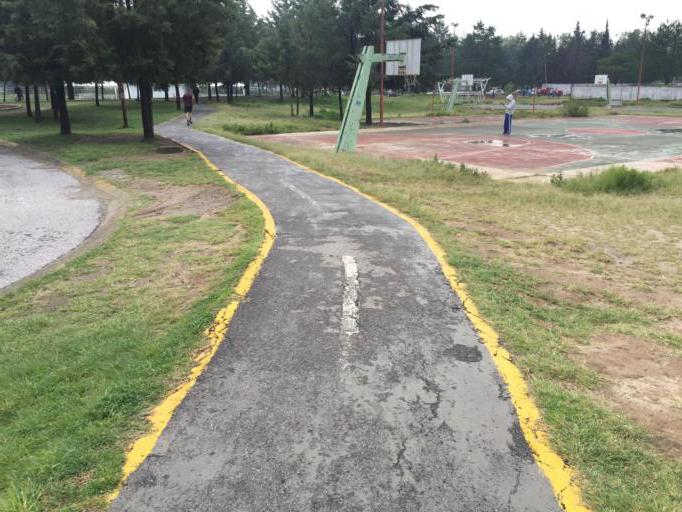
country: MX
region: Mexico
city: Cuautitlan Izcalli
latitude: 19.6496
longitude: -99.2248
